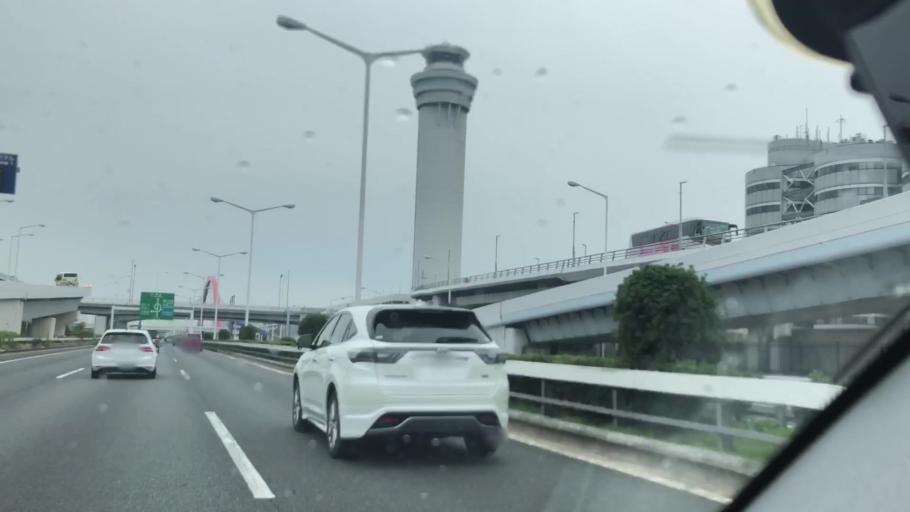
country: JP
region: Kanagawa
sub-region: Kawasaki-shi
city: Kawasaki
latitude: 35.5545
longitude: 139.7832
